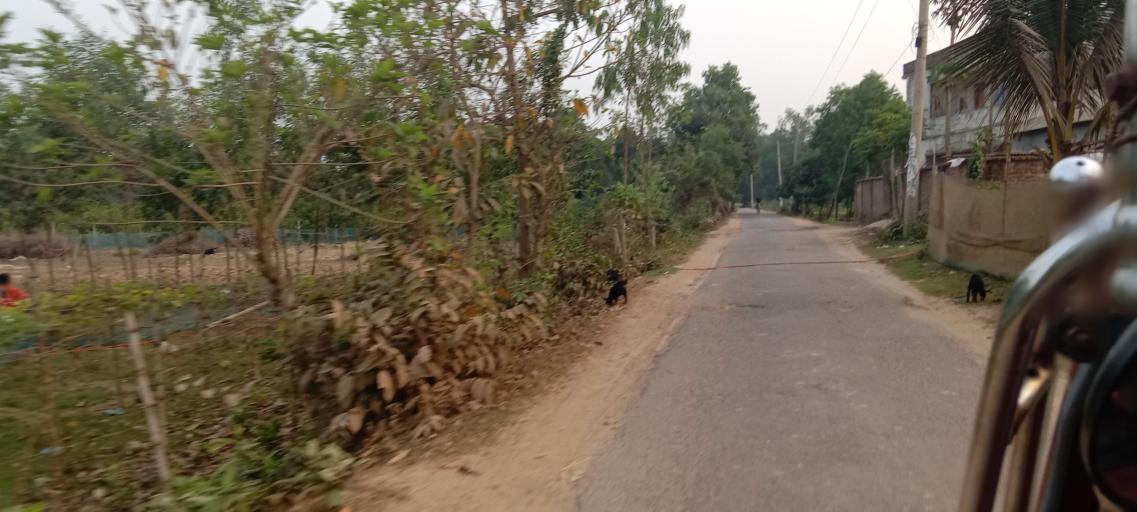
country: BD
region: Dhaka
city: Sakhipur
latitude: 24.4402
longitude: 90.2627
